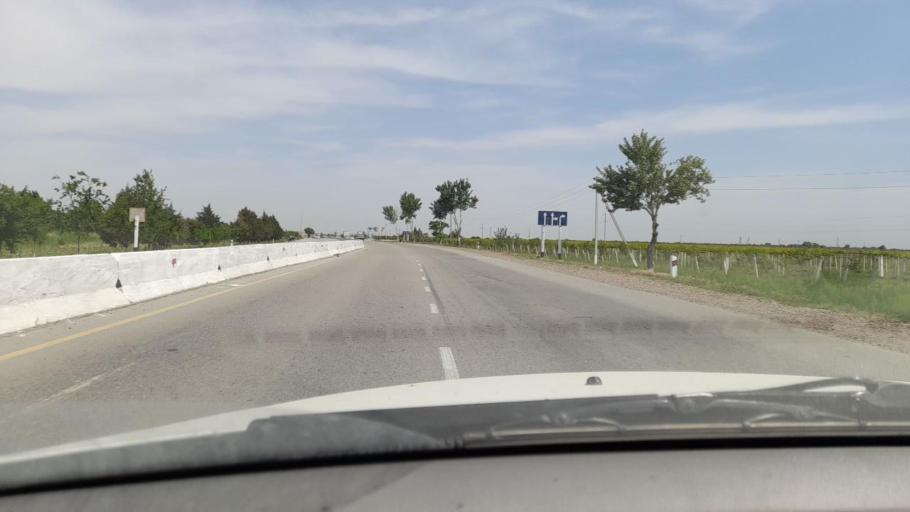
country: UZ
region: Bukhara
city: Galaosiyo
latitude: 39.8976
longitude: 64.4707
